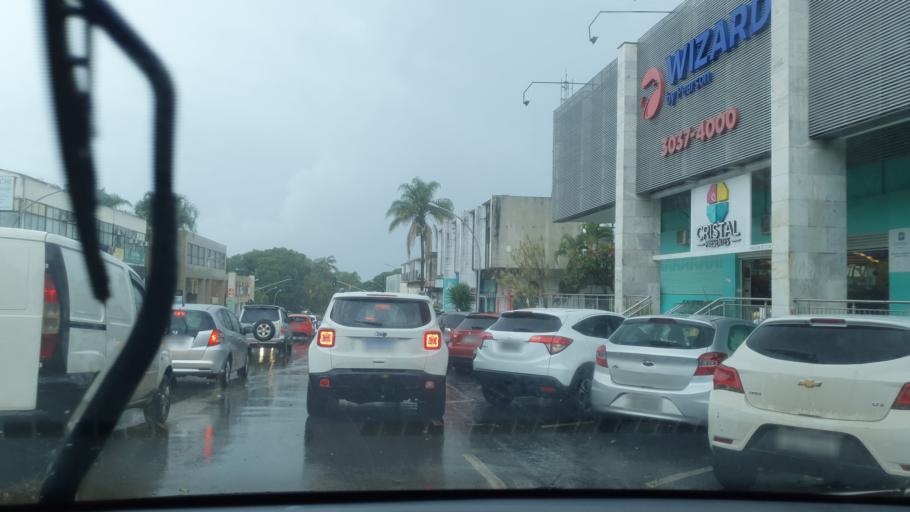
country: BR
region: Federal District
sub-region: Brasilia
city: Brasilia
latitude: -15.7769
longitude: -47.8793
